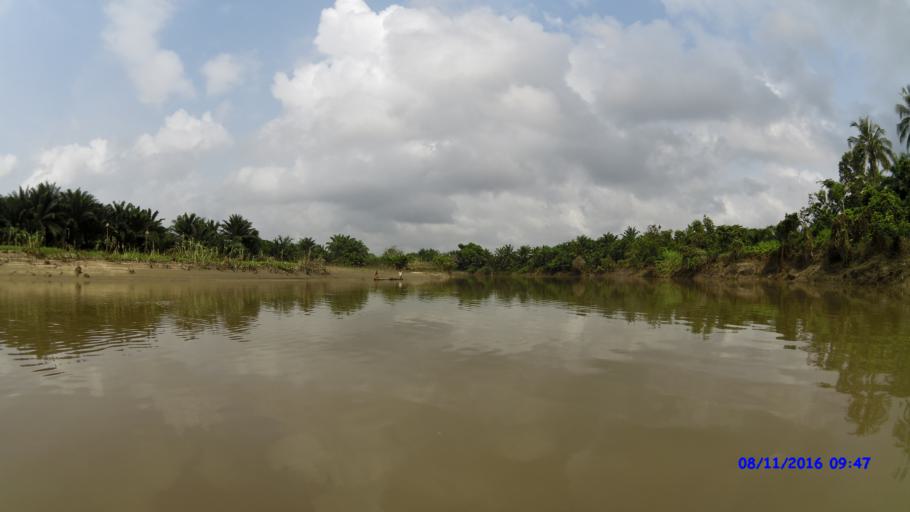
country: BJ
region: Mono
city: Come
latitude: 6.4297
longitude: 1.7733
